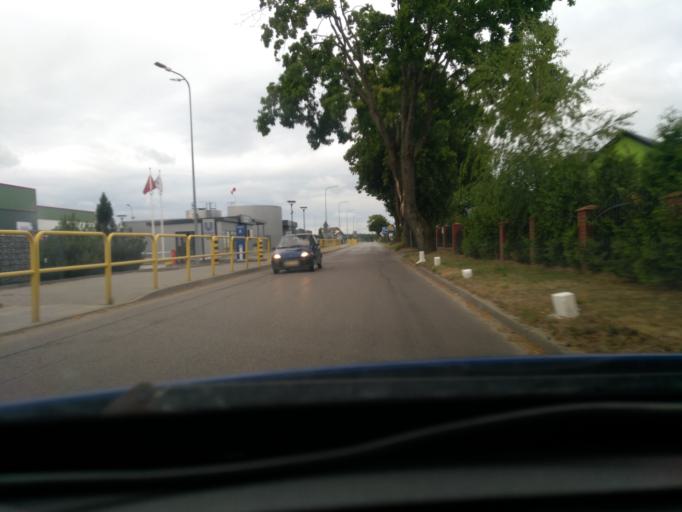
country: PL
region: Pomeranian Voivodeship
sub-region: Powiat kartuski
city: Banino
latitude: 54.3873
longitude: 18.4060
